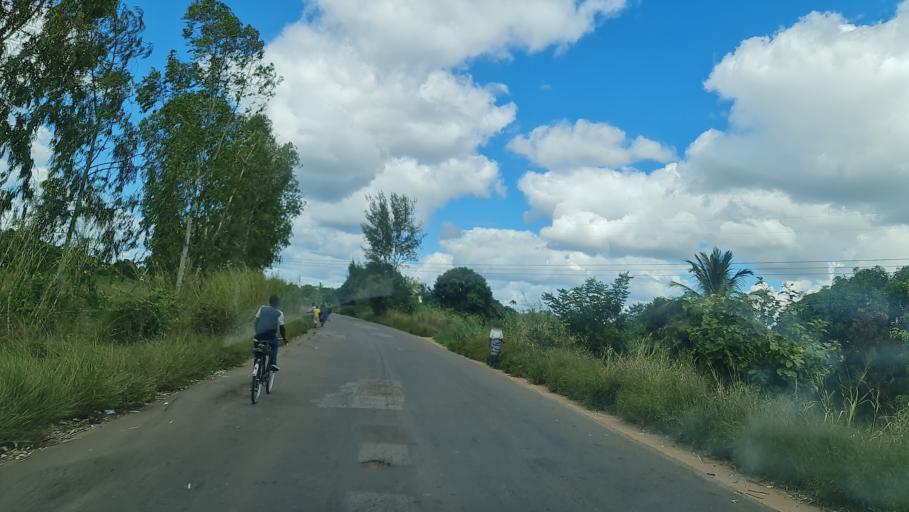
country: MZ
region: Zambezia
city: Quelimane
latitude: -17.5235
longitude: 36.2673
